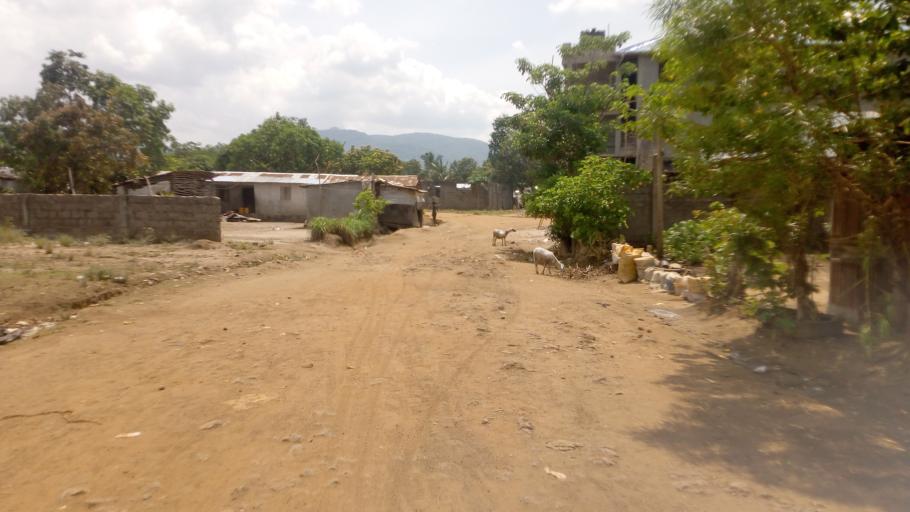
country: SL
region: Western Area
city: Waterloo
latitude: 8.3267
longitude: -13.0780
